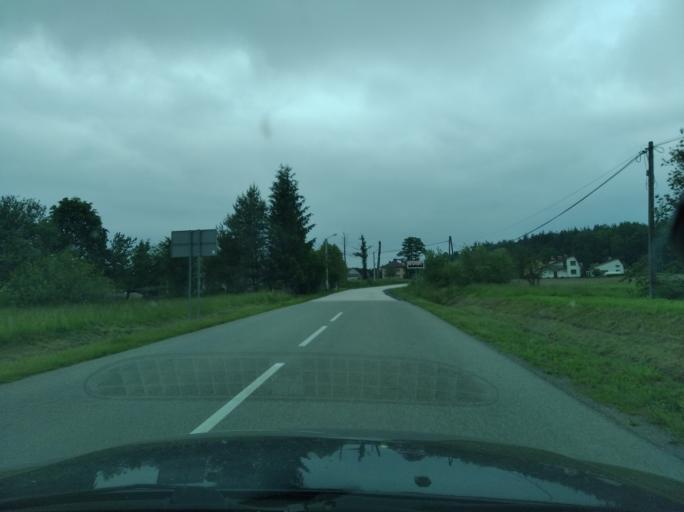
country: PL
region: Subcarpathian Voivodeship
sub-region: Powiat ropczycko-sedziszowski
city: Sedziszow Malopolski
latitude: 50.1109
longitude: 21.6721
